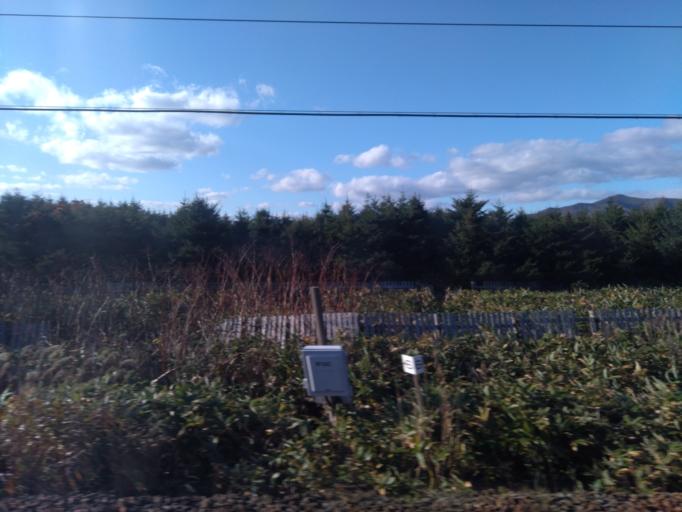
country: JP
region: Hokkaido
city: Niseko Town
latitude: 42.5446
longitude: 140.4108
